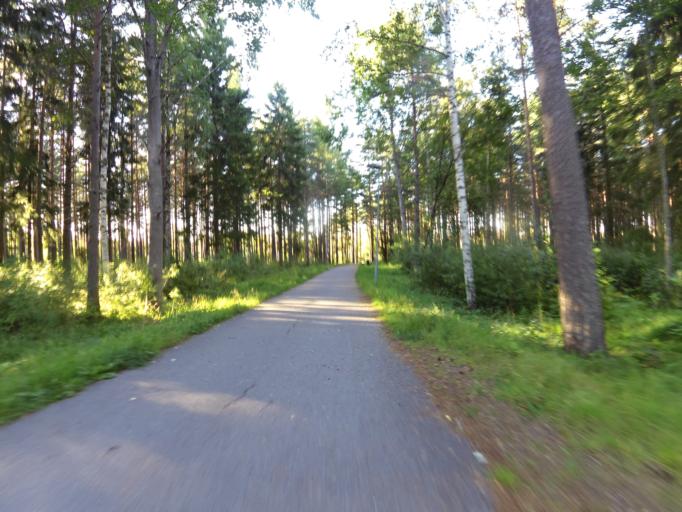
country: SE
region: Gaevleborg
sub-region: Gavle Kommun
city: Gavle
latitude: 60.6481
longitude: 17.1370
